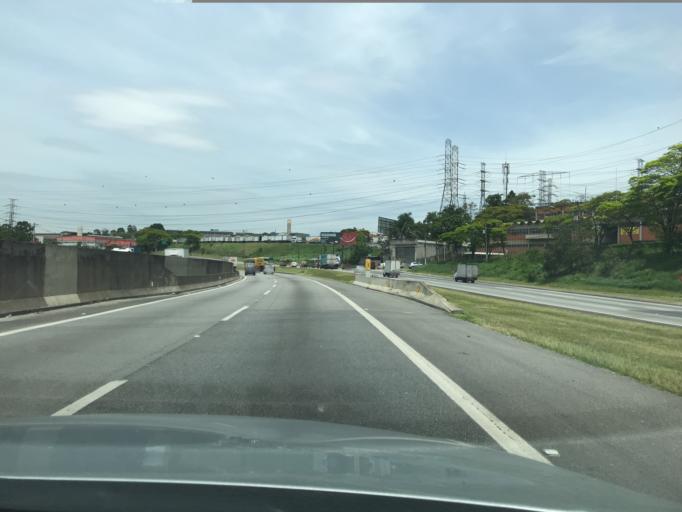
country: BR
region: Sao Paulo
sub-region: Osasco
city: Osasco
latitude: -23.4909
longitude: -46.7667
